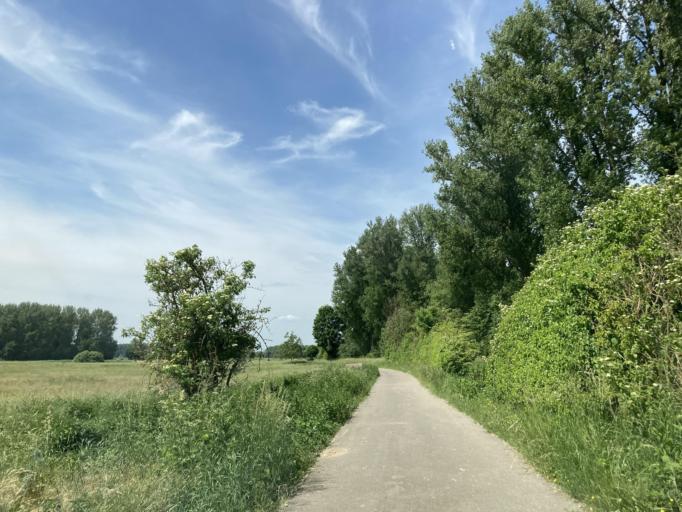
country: DE
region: Baden-Wuerttemberg
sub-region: Karlsruhe Region
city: Graben-Neudorf
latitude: 49.1707
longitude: 8.4695
